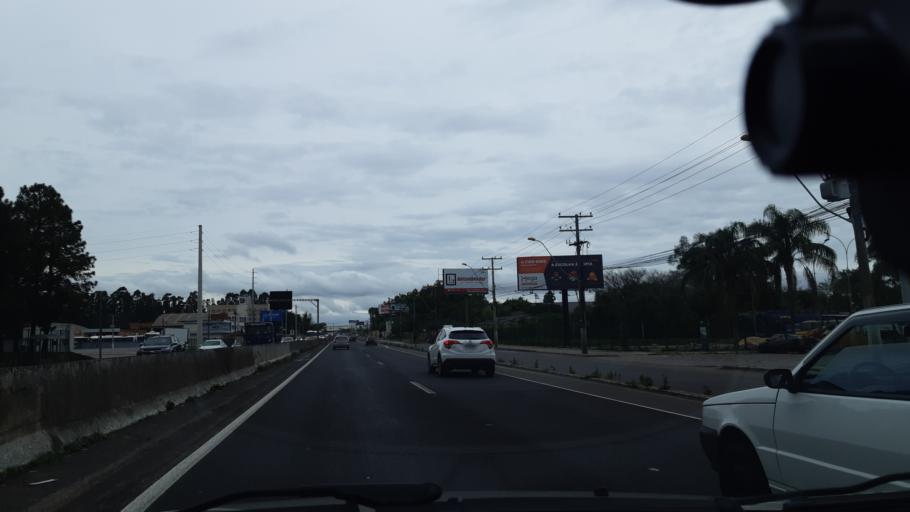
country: BR
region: Rio Grande do Sul
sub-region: Esteio
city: Esteio
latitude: -29.8367
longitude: -51.1754
